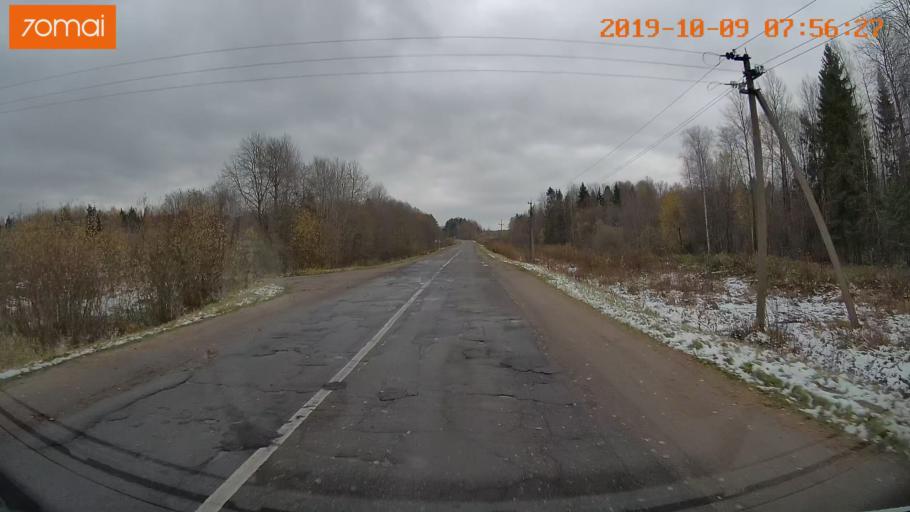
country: RU
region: Jaroslavl
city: Kukoboy
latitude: 58.6979
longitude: 39.9353
